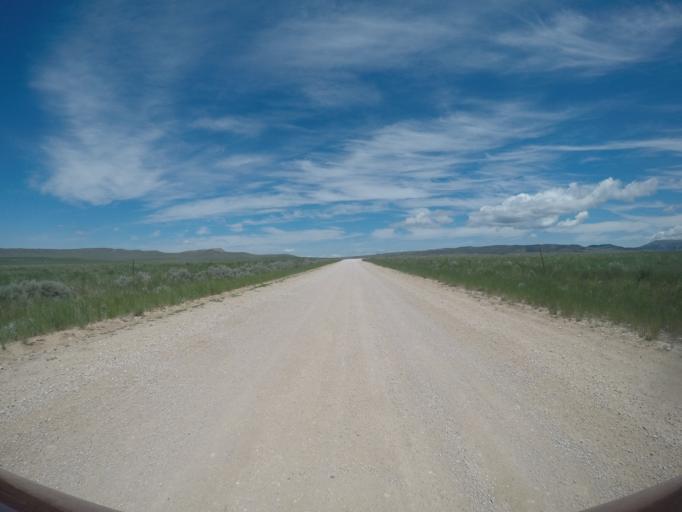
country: US
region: Montana
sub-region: Yellowstone County
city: Laurel
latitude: 45.2181
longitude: -108.7191
